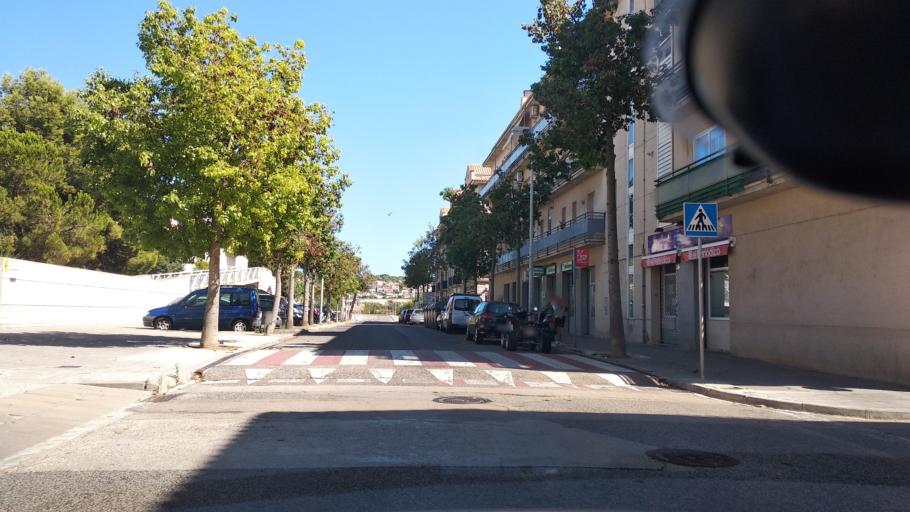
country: ES
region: Catalonia
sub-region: Provincia de Tarragona
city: El Vendrell
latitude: 41.2194
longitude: 1.5388
